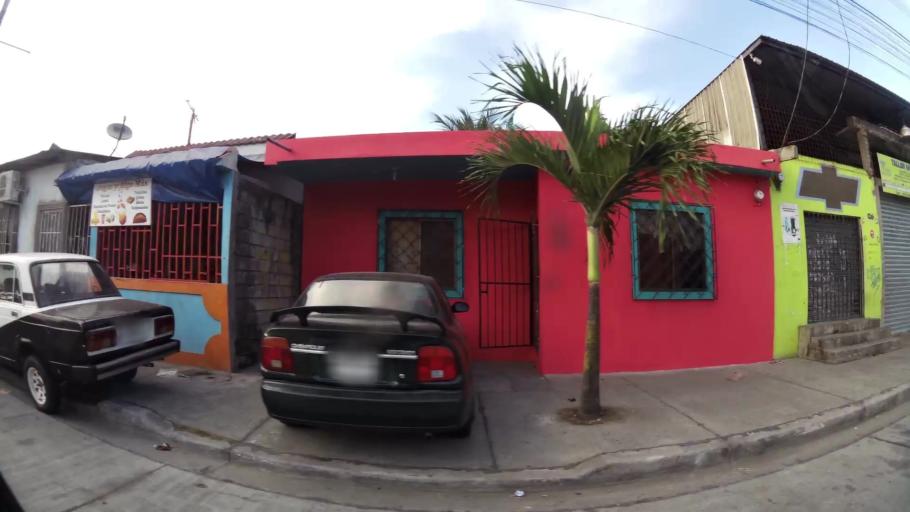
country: EC
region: Guayas
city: Eloy Alfaro
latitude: -2.0912
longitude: -79.9052
